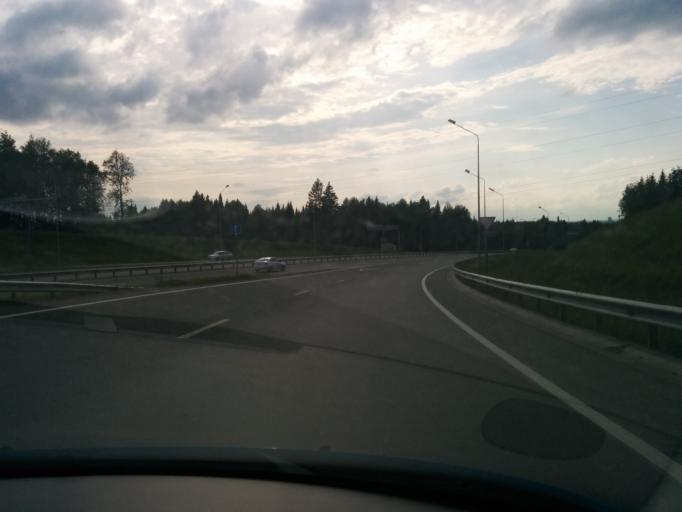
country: RU
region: Perm
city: Ferma
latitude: 57.9995
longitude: 56.3834
